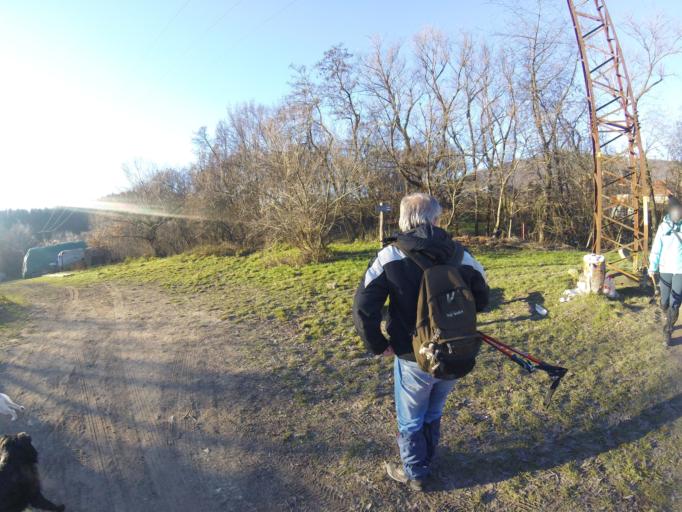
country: HU
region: Pest
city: Pilisszentkereszt
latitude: 47.6894
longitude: 18.9053
